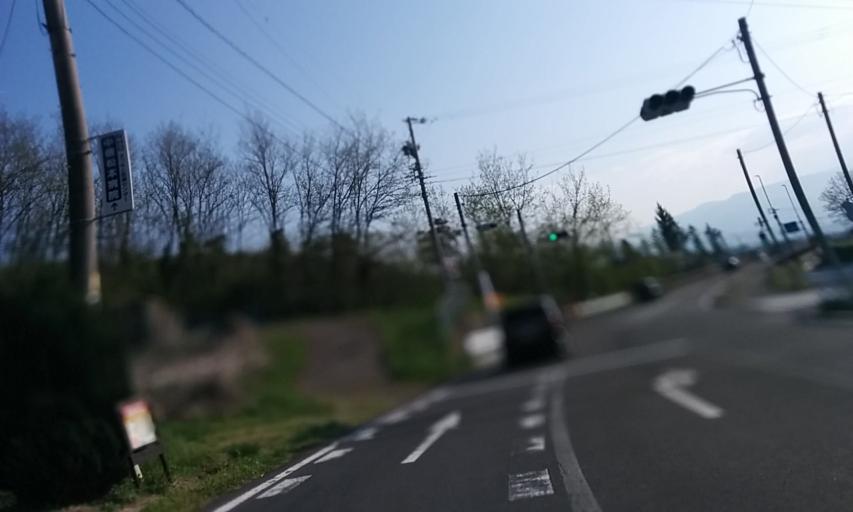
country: JP
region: Nagano
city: Matsumoto
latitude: 36.1727
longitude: 137.9995
